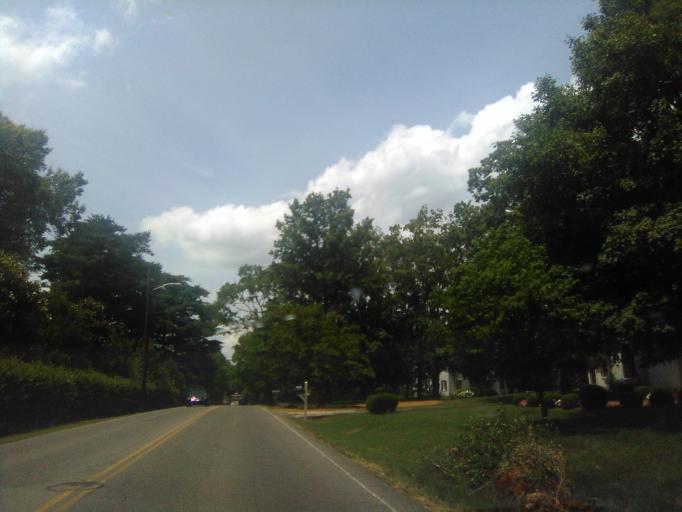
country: US
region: Tennessee
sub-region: Davidson County
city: Belle Meade
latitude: 36.0976
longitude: -86.8642
